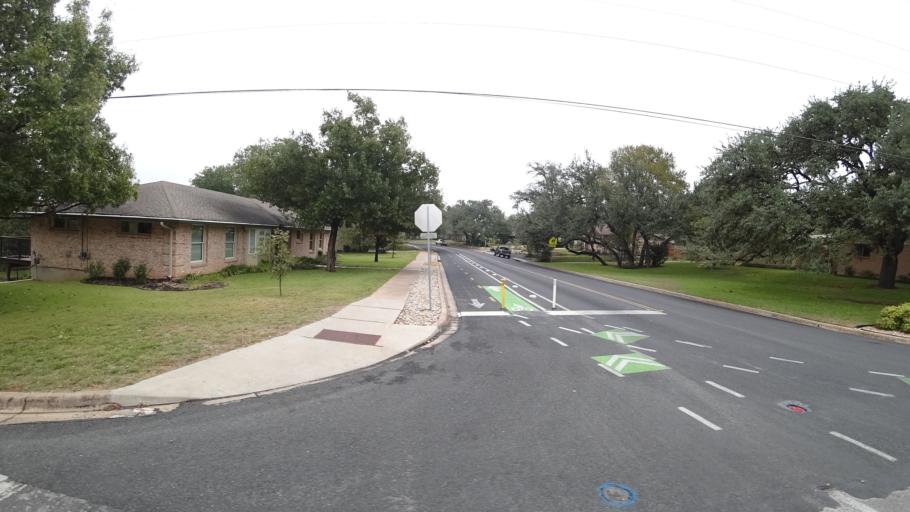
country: US
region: Texas
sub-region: Travis County
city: Rollingwood
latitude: 30.2530
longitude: -97.7852
